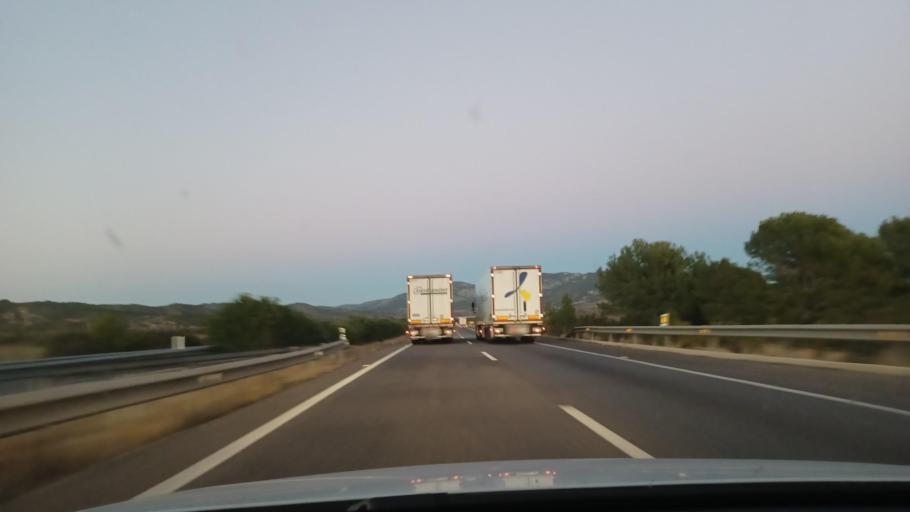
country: ES
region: Valencia
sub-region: Provincia de Castello
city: Torreblanca
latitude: 40.2398
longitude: 0.2186
